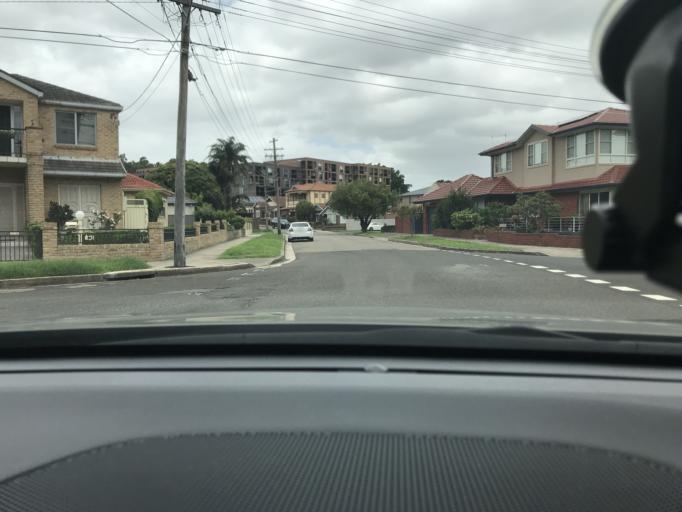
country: AU
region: New South Wales
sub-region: Canada Bay
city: Wareemba
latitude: -33.8624
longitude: 151.1288
